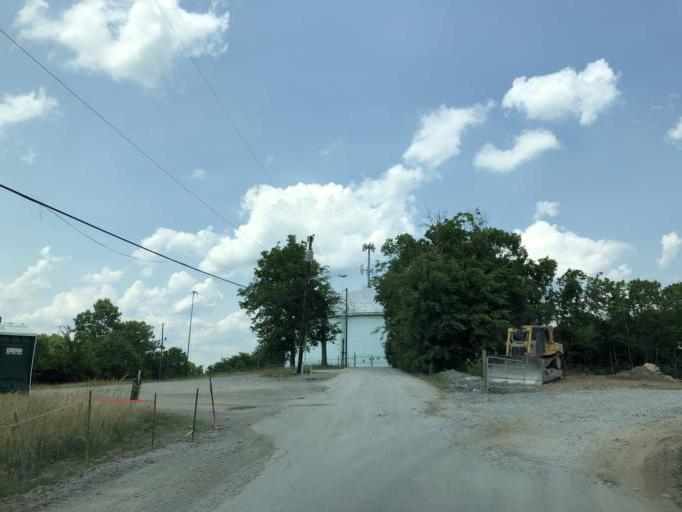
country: US
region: Tennessee
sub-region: Davidson County
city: Goodlettsville
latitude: 36.2665
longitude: -86.7362
